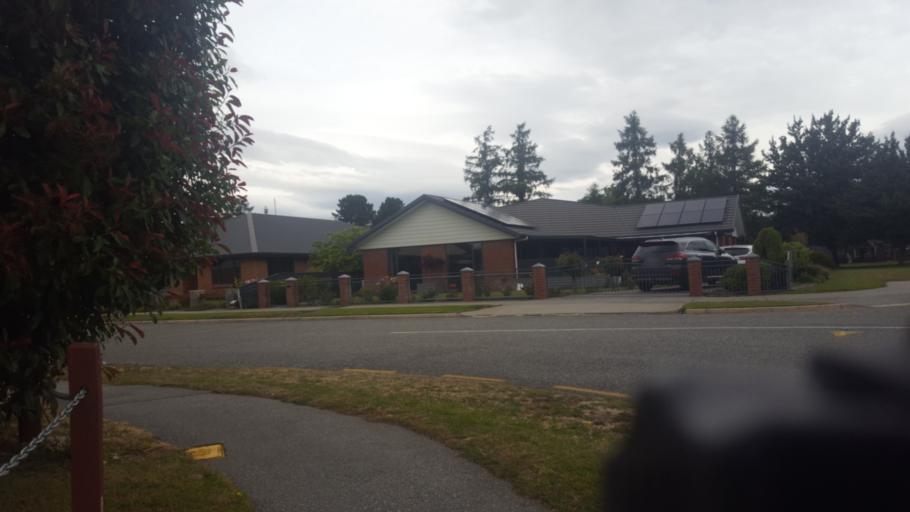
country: NZ
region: Otago
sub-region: Queenstown-Lakes District
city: Wanaka
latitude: -45.0435
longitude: 169.1868
